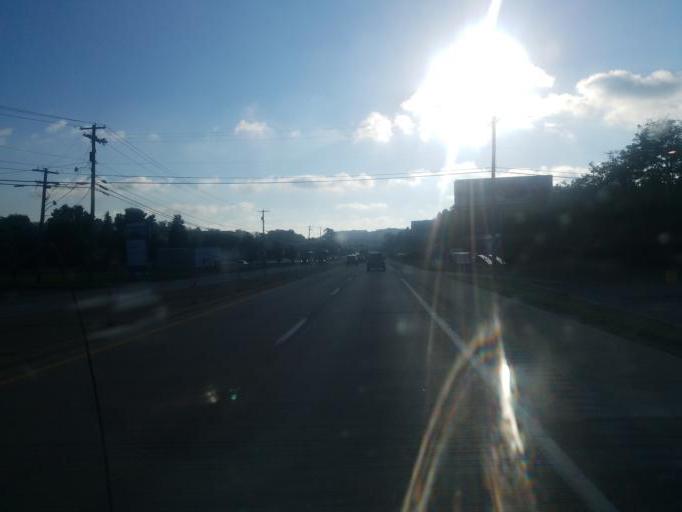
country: US
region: Pennsylvania
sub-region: Westmoreland County
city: Delmont
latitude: 40.4000
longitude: -79.5838
